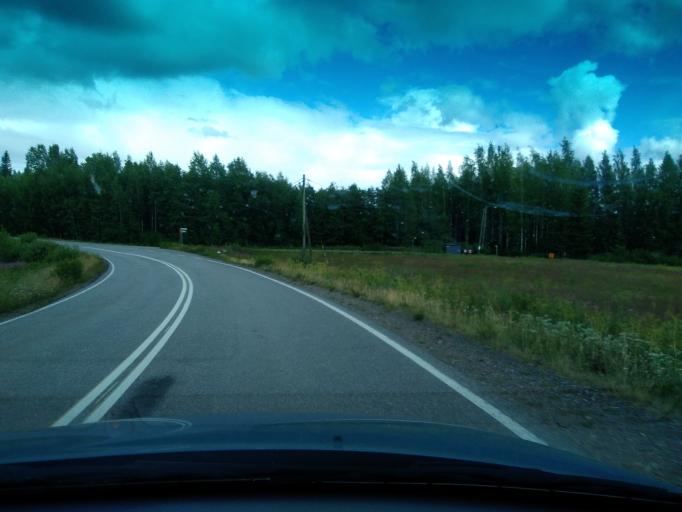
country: FI
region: Central Finland
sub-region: Saarijaervi-Viitasaari
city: Saarijaervi
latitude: 62.7325
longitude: 25.1568
